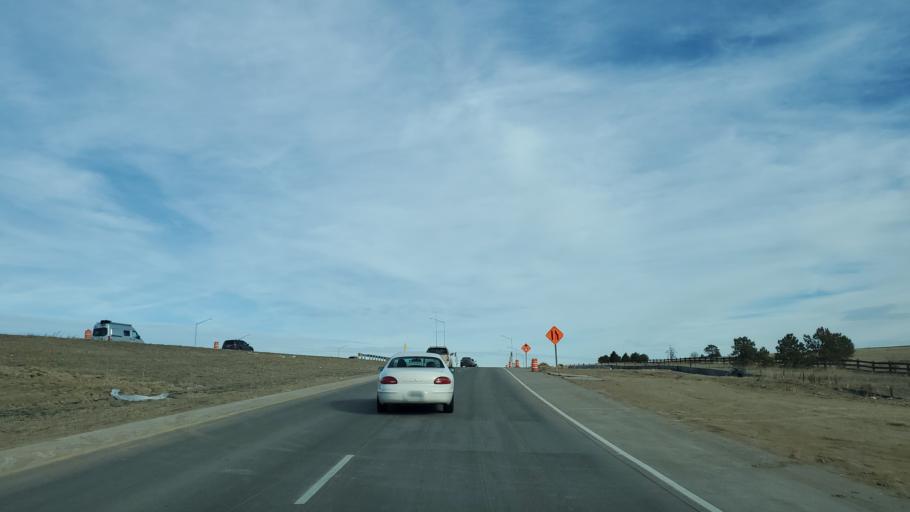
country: US
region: Colorado
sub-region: Douglas County
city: Highlands Ranch
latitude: 39.5627
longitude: -104.9590
